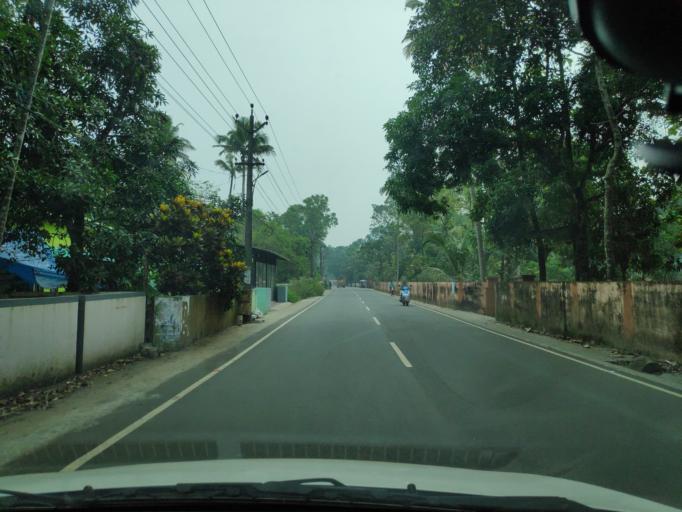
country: IN
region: Kerala
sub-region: Alappuzha
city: Shertallai
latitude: 9.6084
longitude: 76.3383
